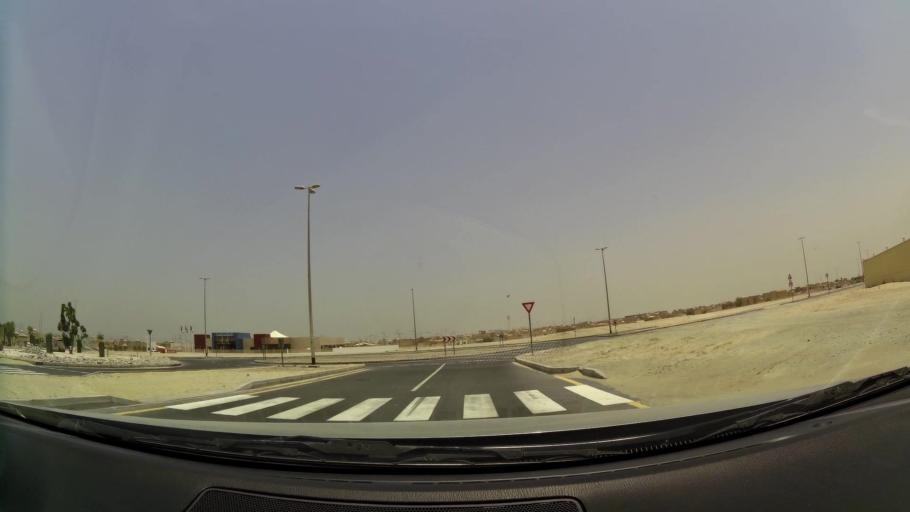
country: AE
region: Dubai
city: Dubai
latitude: 25.0846
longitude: 55.2406
